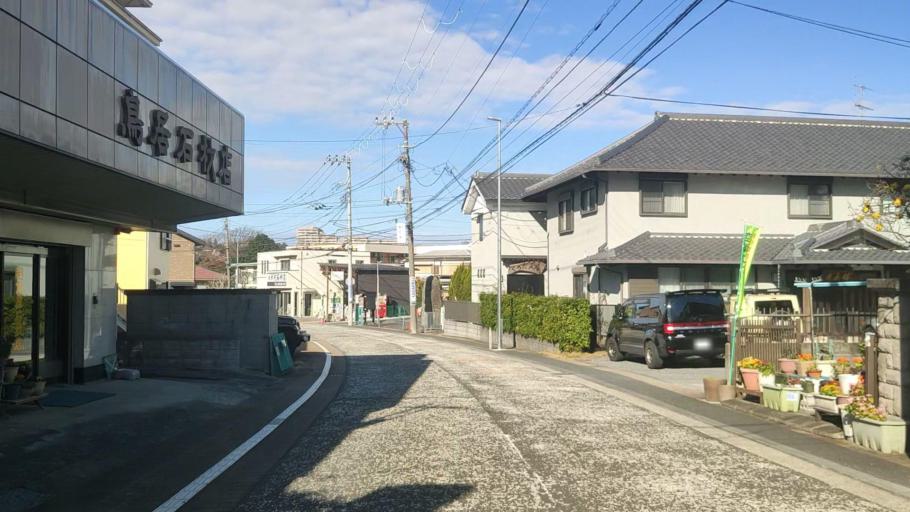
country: JP
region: Kanagawa
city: Yokohama
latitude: 35.3921
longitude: 139.5864
